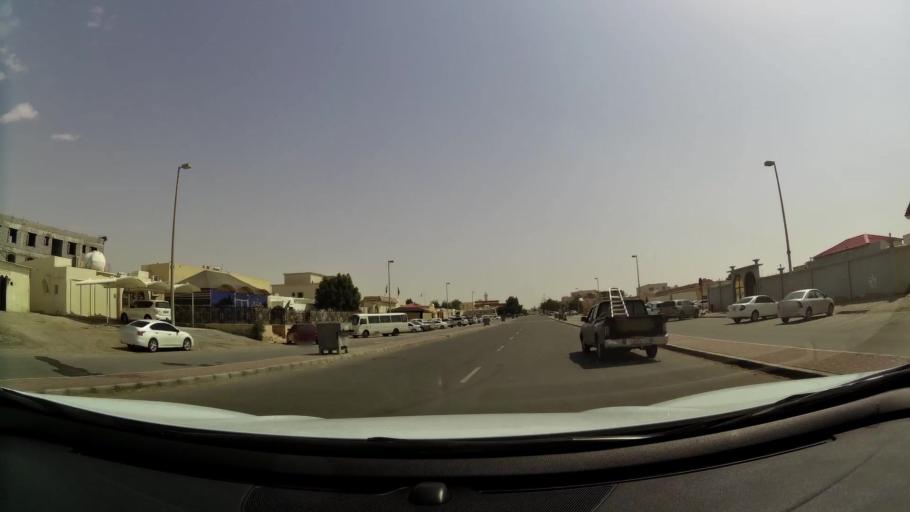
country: AE
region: Abu Dhabi
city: Abu Dhabi
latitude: 24.2915
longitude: 54.6522
